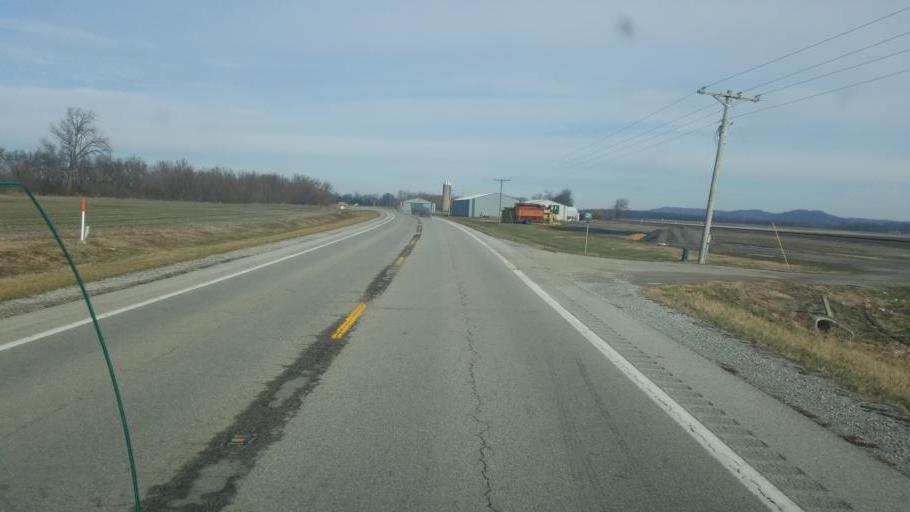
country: US
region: Missouri
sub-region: Cape Girardeau County
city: Cape Girardeau
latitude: 37.3485
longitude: -89.4019
